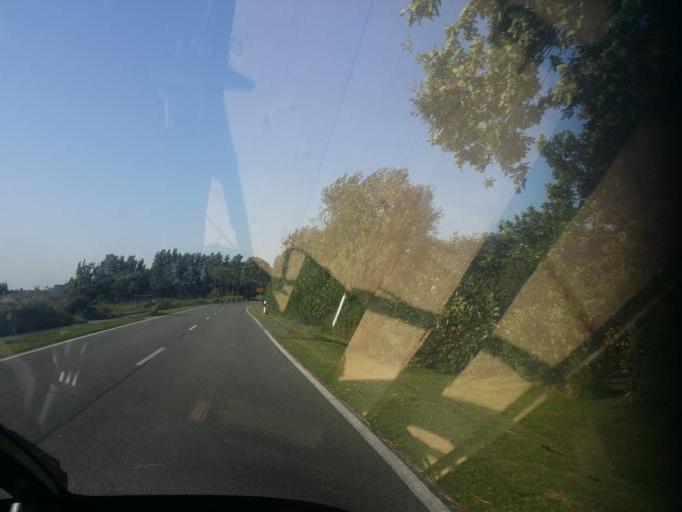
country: DE
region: Schleswig-Holstein
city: Neukirchen
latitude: 54.8758
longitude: 8.7400
